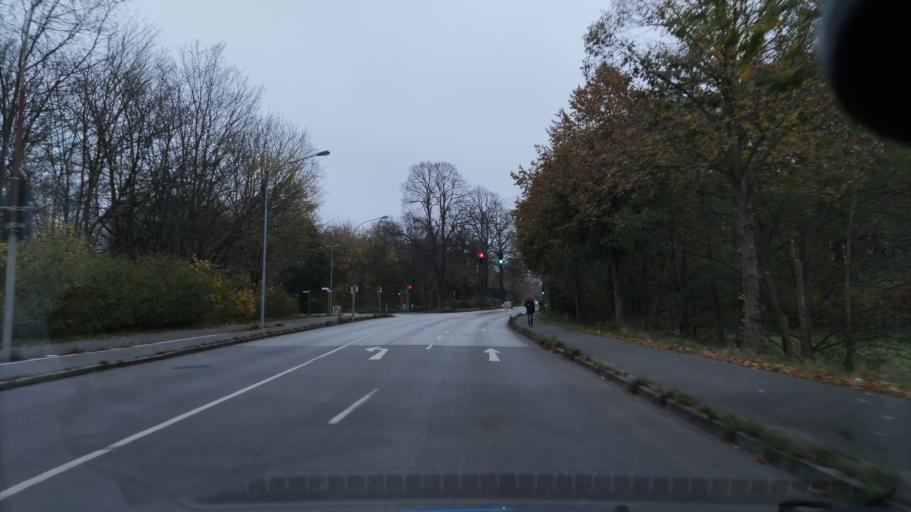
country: DE
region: Schleswig-Holstein
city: Luebeck
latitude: 53.8335
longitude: 10.7158
